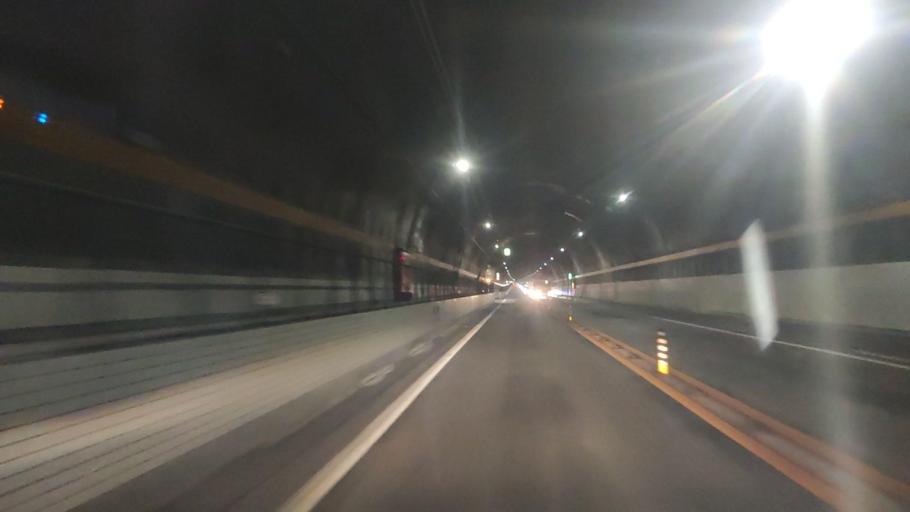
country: JP
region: Nagasaki
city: Obita
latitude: 32.7881
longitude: 129.8823
